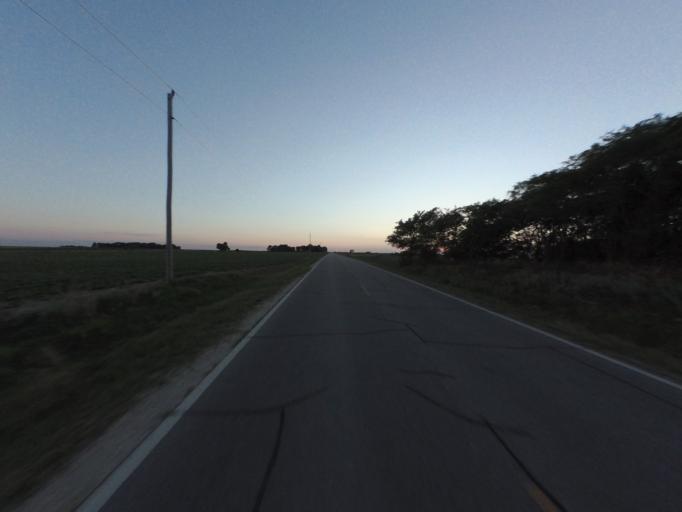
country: US
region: Kansas
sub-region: Rice County
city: Sterling
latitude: 38.1446
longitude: -98.1907
